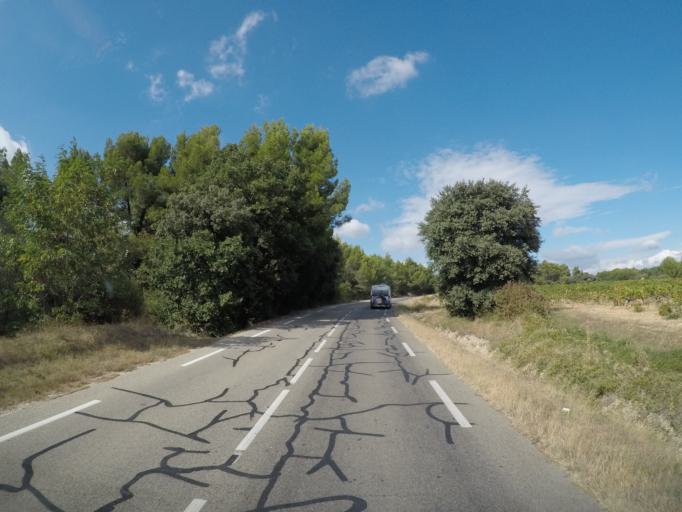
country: FR
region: Provence-Alpes-Cote d'Azur
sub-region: Departement du Vaucluse
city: Vaison-la-Romaine
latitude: 44.2649
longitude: 5.0195
